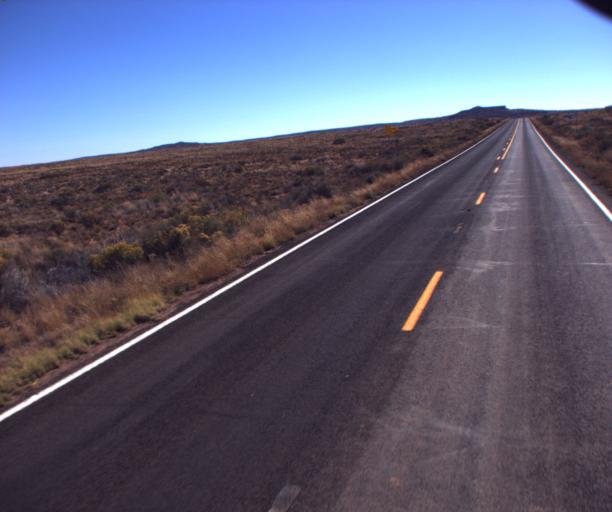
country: US
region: Arizona
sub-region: Navajo County
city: First Mesa
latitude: 35.9795
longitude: -110.7035
